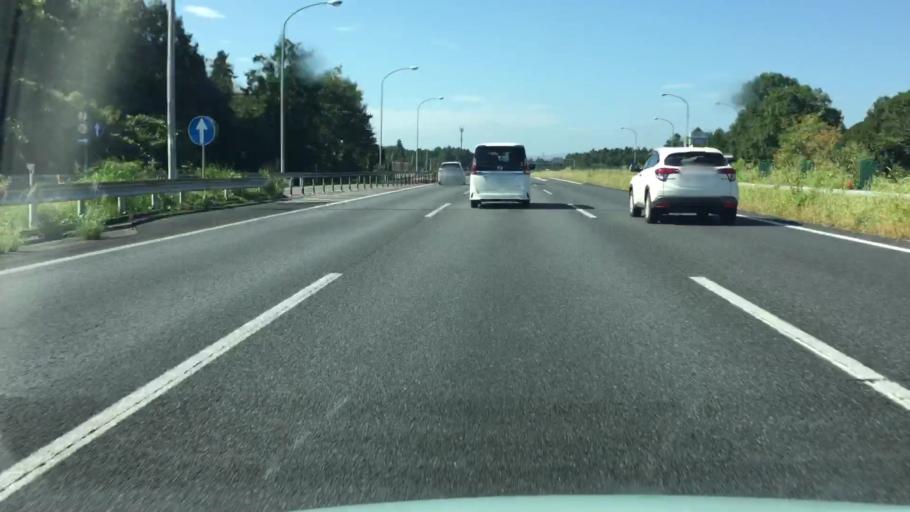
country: JP
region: Ibaraki
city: Tomobe
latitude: 36.2817
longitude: 140.3189
